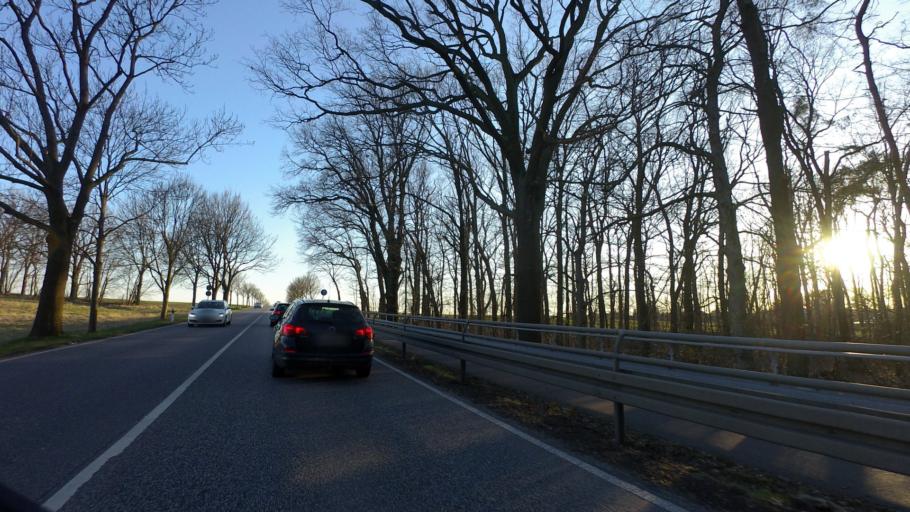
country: DE
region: Brandenburg
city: Ahrensfelde
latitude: 52.5879
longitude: 13.5922
